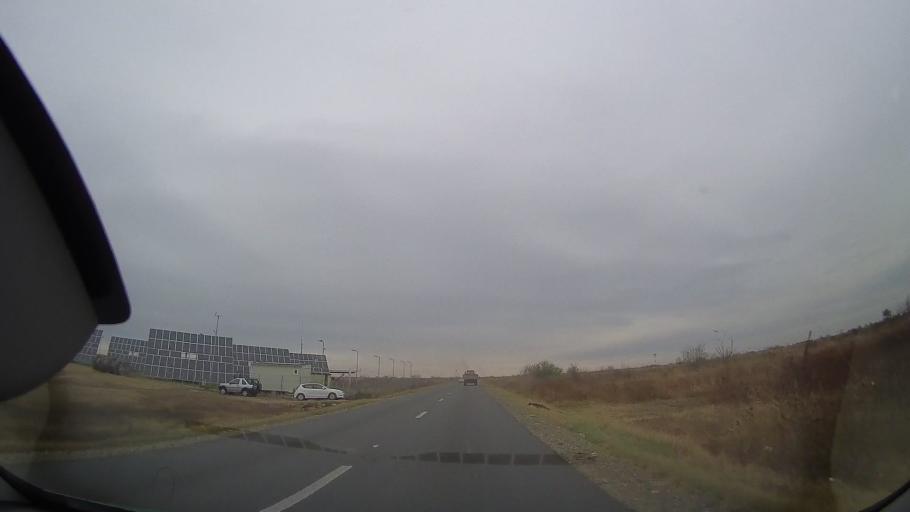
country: RO
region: Ialomita
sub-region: Oras Amara
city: Amara
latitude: 44.6262
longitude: 27.3012
